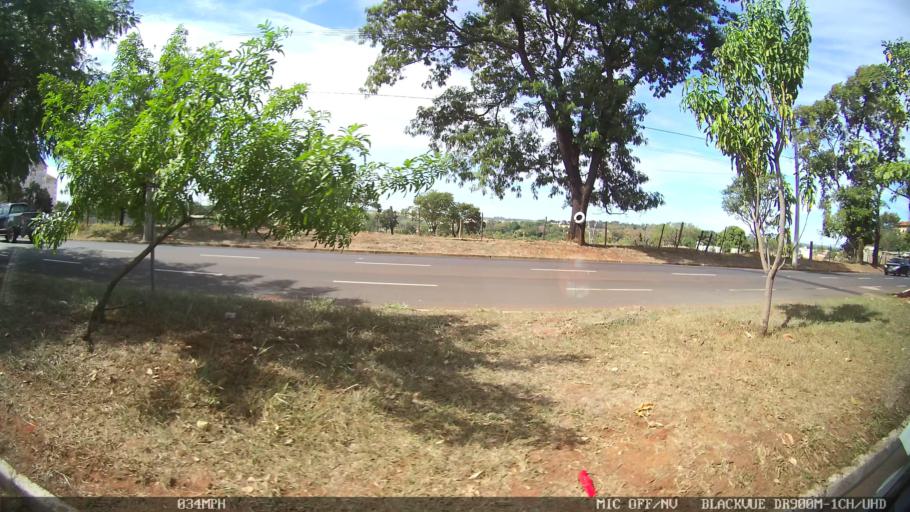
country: BR
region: Sao Paulo
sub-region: Sao Jose Do Rio Preto
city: Sao Jose do Rio Preto
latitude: -20.8290
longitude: -49.3512
